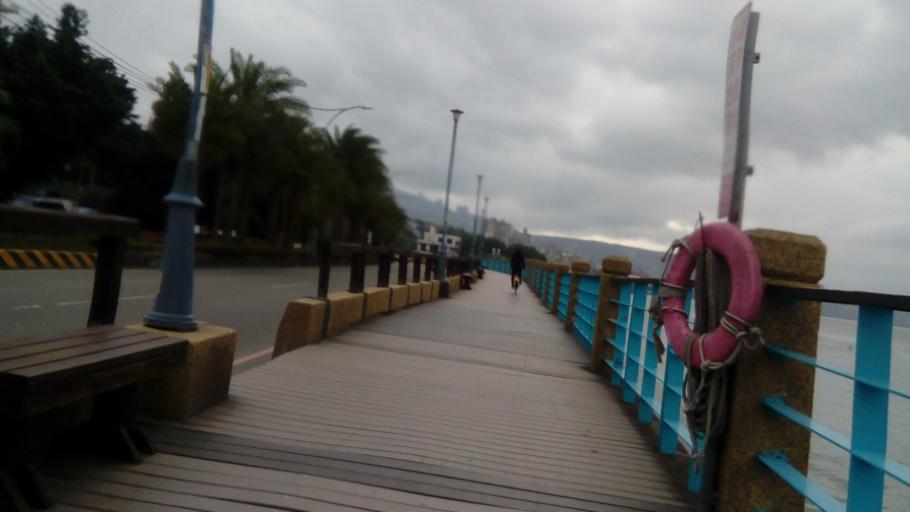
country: TW
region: Taipei
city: Taipei
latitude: 25.1756
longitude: 121.4284
